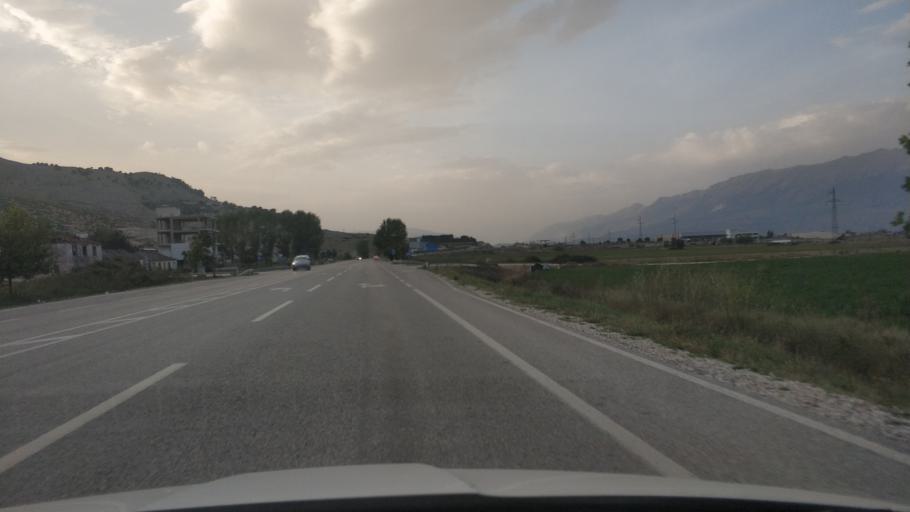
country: AL
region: Gjirokaster
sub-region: Rrethi i Gjirokastres
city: Libohove
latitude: 39.9666
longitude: 20.2400
